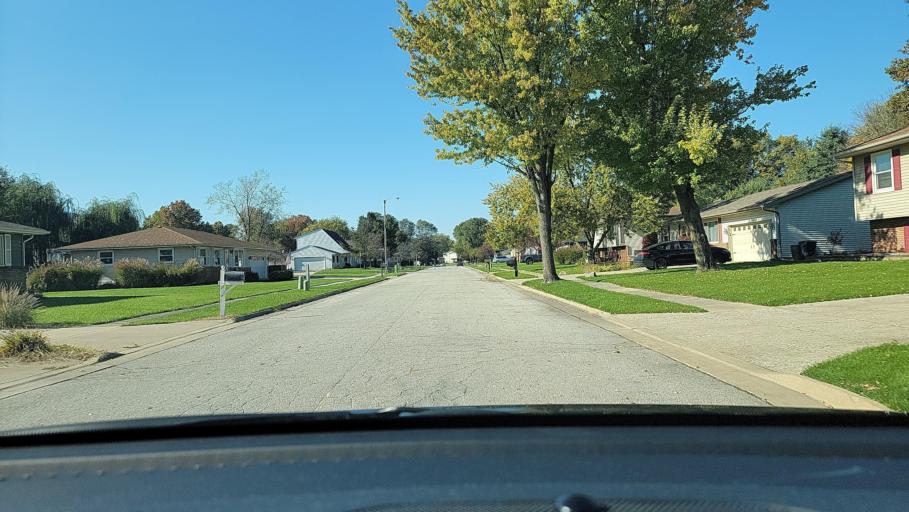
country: US
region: Indiana
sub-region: Porter County
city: Portage
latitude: 41.5821
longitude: -87.1598
